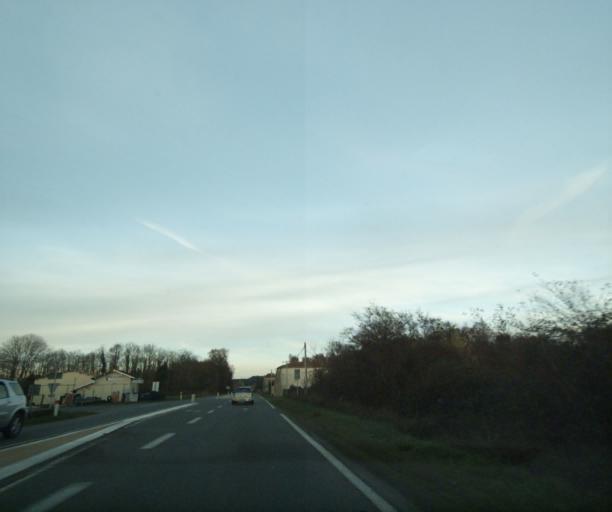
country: FR
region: Aquitaine
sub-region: Departement de la Gironde
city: Bazas
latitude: 44.4677
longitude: -0.2295
